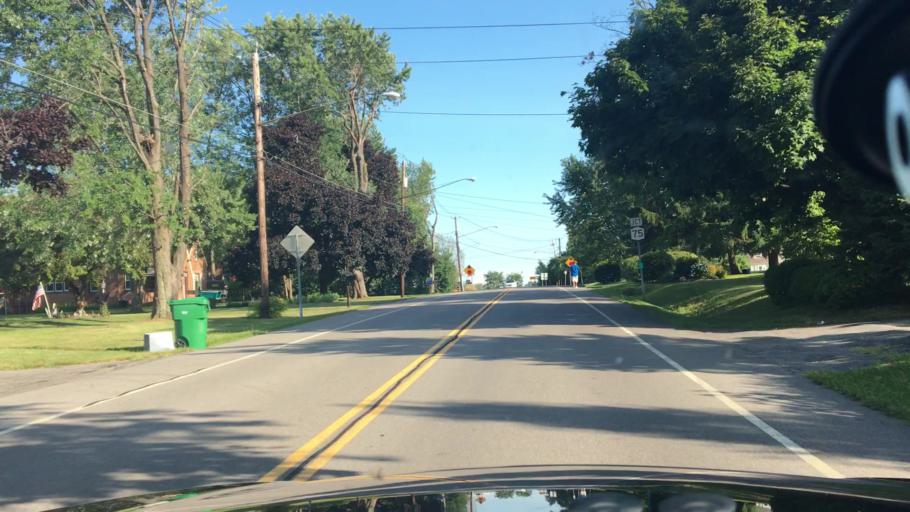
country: US
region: New York
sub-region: Erie County
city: Wanakah
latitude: 42.7687
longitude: -78.8666
